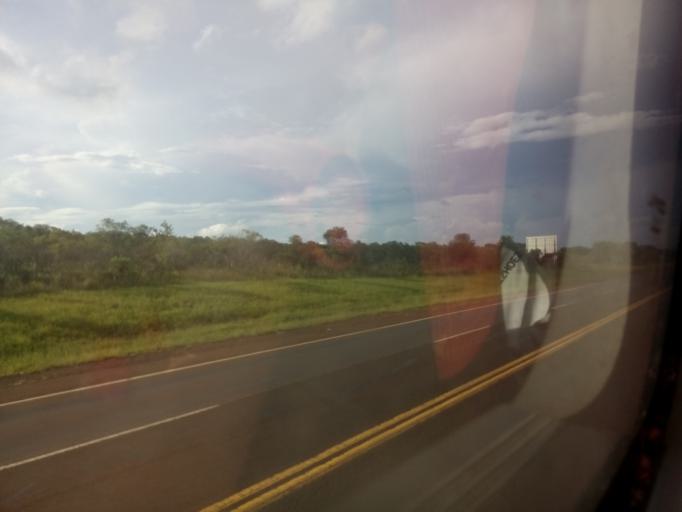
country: AR
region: Misiones
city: Santa Ana
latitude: -27.4146
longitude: -55.6115
